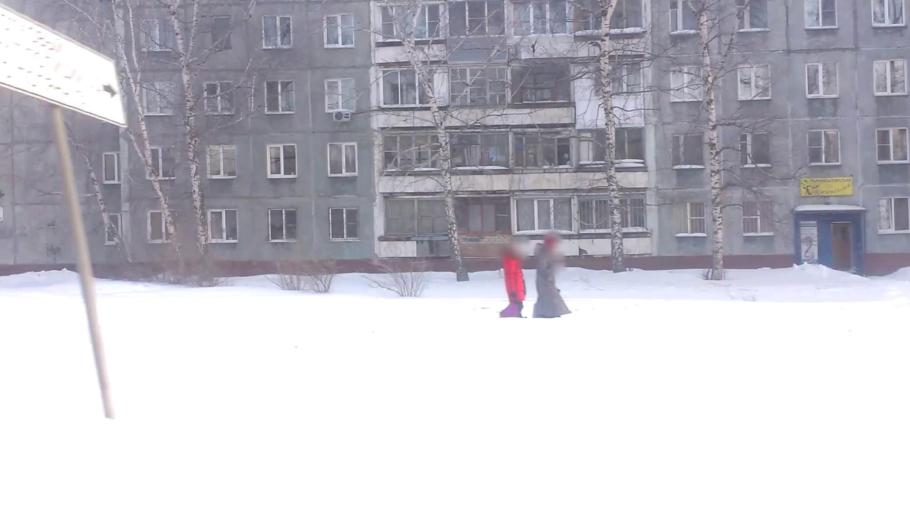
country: RU
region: Altai Krai
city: Novosilikatnyy
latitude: 53.3701
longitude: 83.6622
